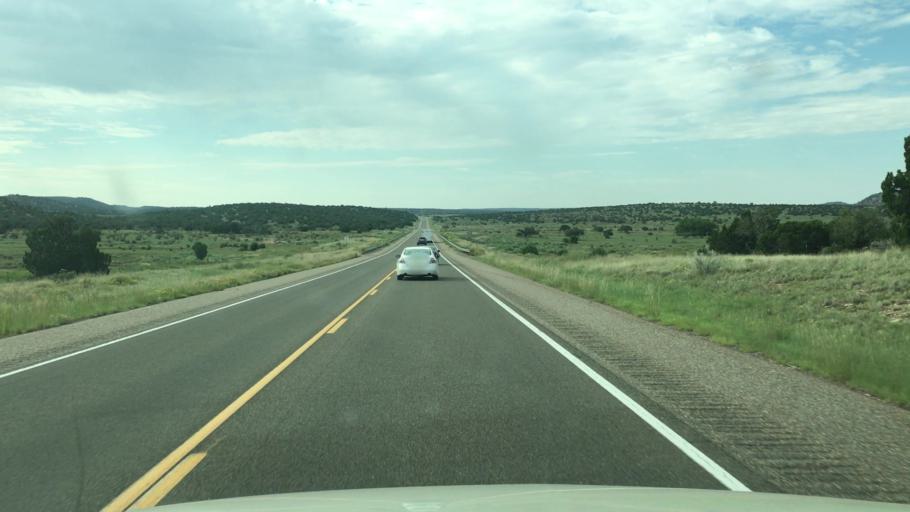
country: US
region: New Mexico
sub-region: Santa Fe County
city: Eldorado at Santa Fe
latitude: 35.3103
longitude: -105.8295
